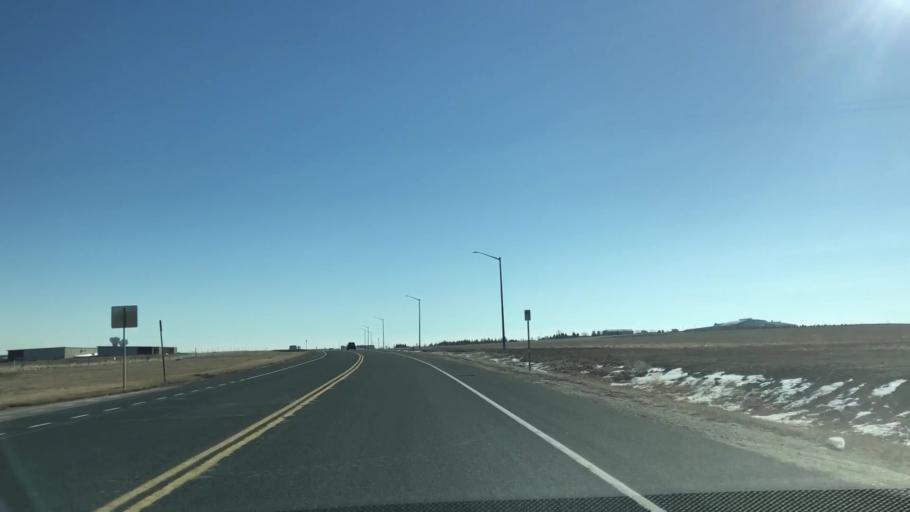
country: US
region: Colorado
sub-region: Weld County
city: Windsor
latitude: 40.4563
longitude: -104.9828
